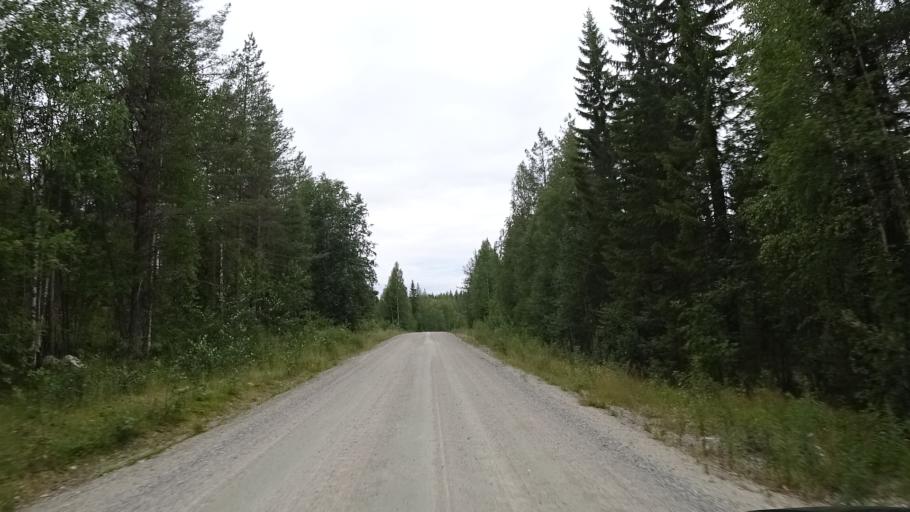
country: FI
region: North Karelia
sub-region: Joensuu
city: Eno
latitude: 63.1568
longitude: 30.5955
